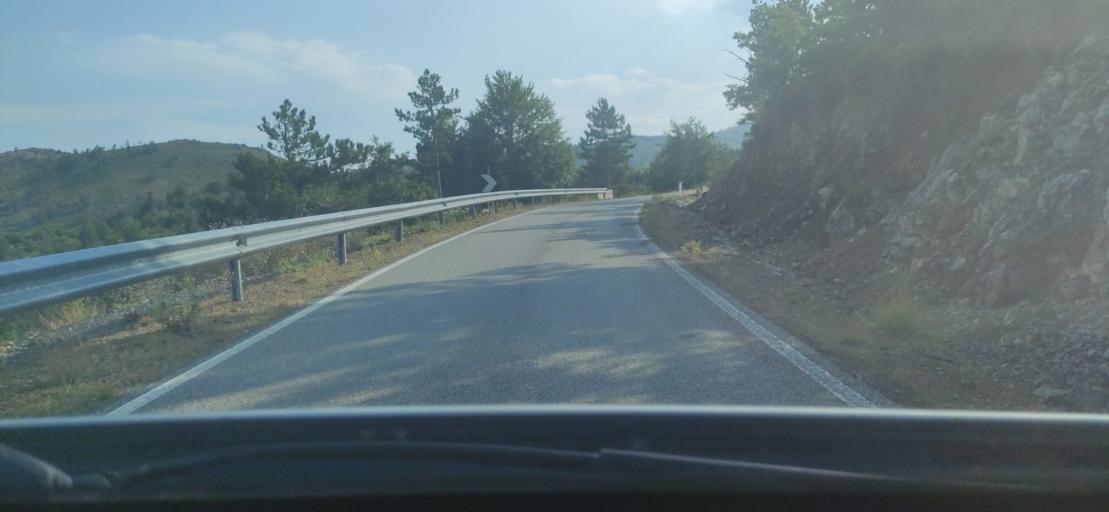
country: AL
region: Shkoder
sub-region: Rrethi i Pukes
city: Iballe
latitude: 42.1711
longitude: 20.0210
